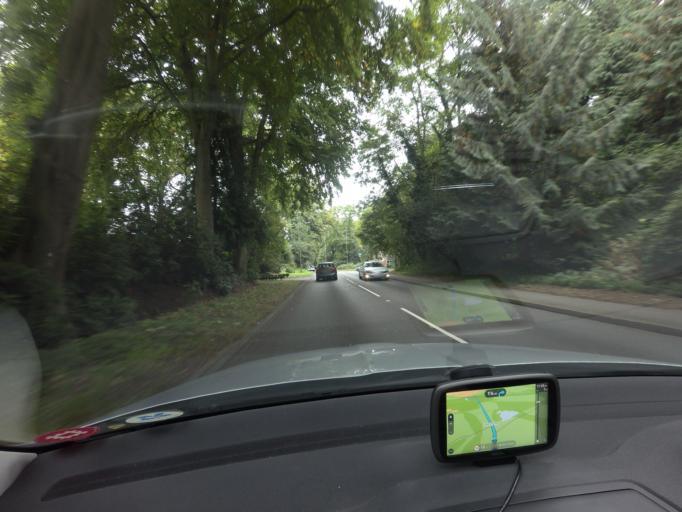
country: GB
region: England
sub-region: Surrey
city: Byfleet
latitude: 51.3394
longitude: -0.4526
